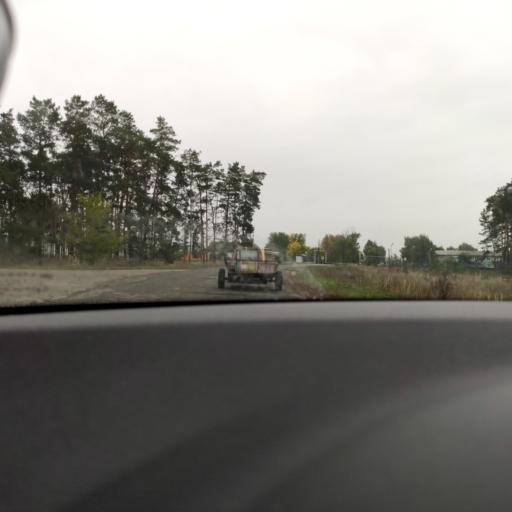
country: RU
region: Samara
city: Yelkhovka
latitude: 53.7387
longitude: 50.3096
